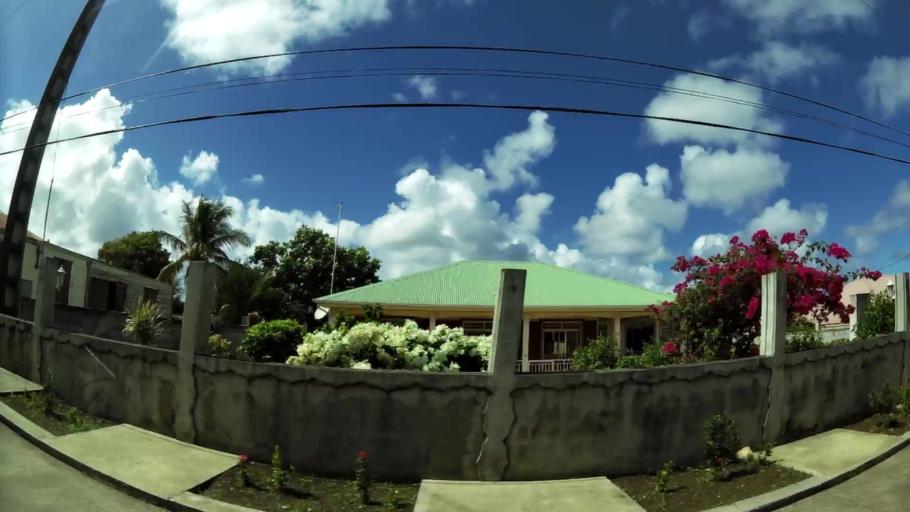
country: GP
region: Guadeloupe
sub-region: Guadeloupe
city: Anse-Bertrand
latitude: 16.4505
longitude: -61.4781
